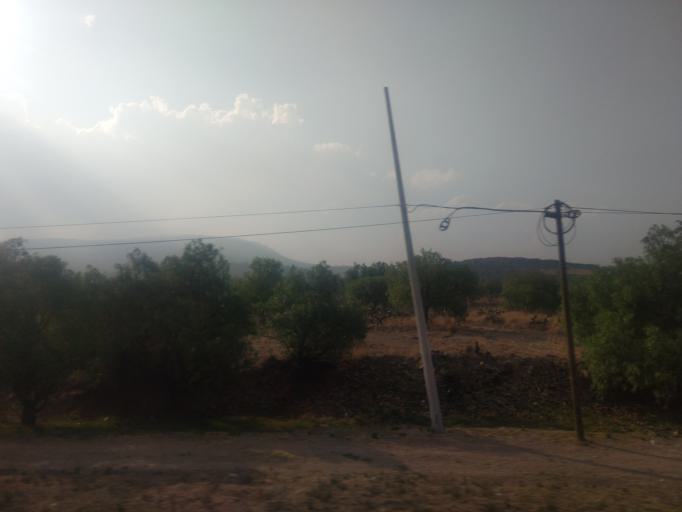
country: MX
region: Mexico
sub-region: Axapusco
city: Colonia los Remedios
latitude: 19.7320
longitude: -98.7759
